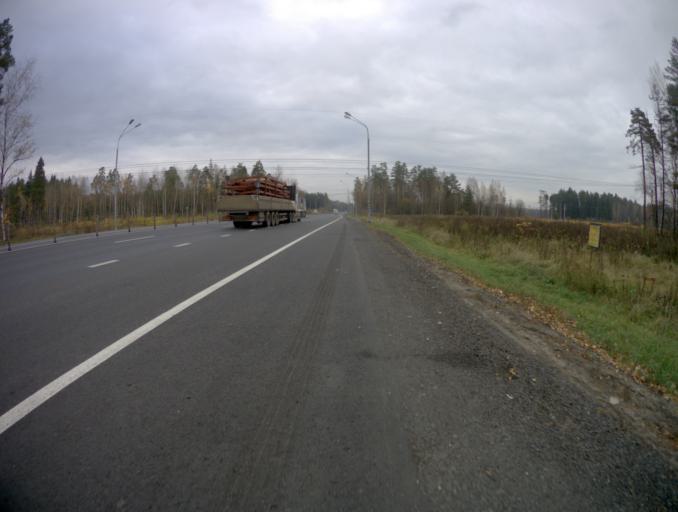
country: RU
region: Moskovskaya
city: Malaya Dubna
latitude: 55.8504
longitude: 38.9639
